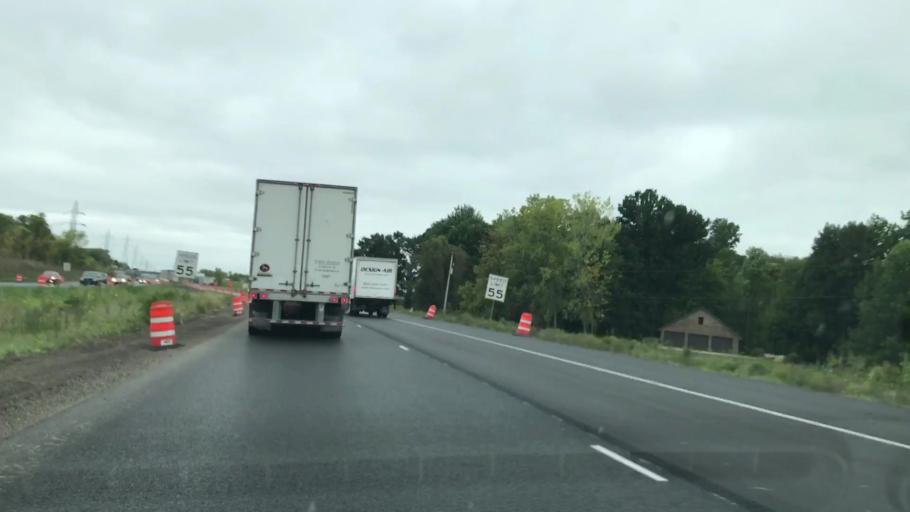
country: US
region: Wisconsin
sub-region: Brown County
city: Suamico
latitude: 44.6275
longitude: -88.0499
